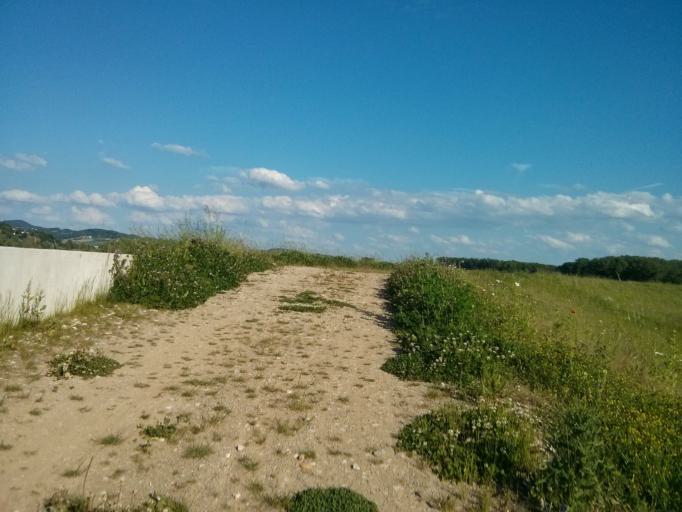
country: DE
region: Bavaria
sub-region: Lower Bavaria
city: Metten
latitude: 48.8398
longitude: 12.9135
